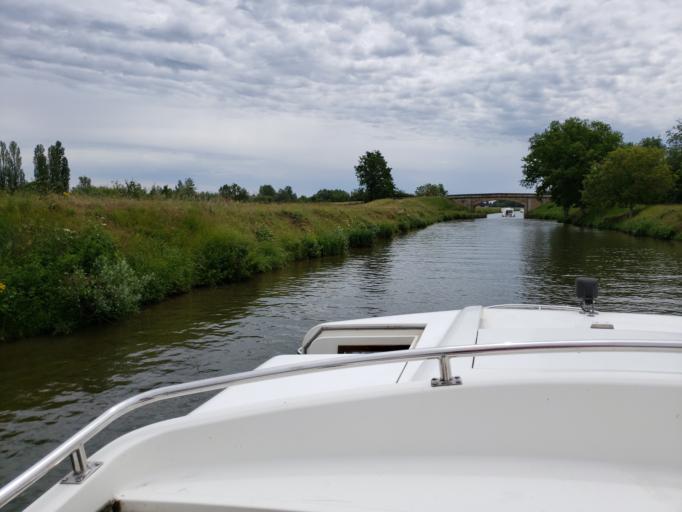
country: FR
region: Bourgogne
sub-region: Departement de l'Yonne
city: Gurgy
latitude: 47.8812
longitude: 3.5479
